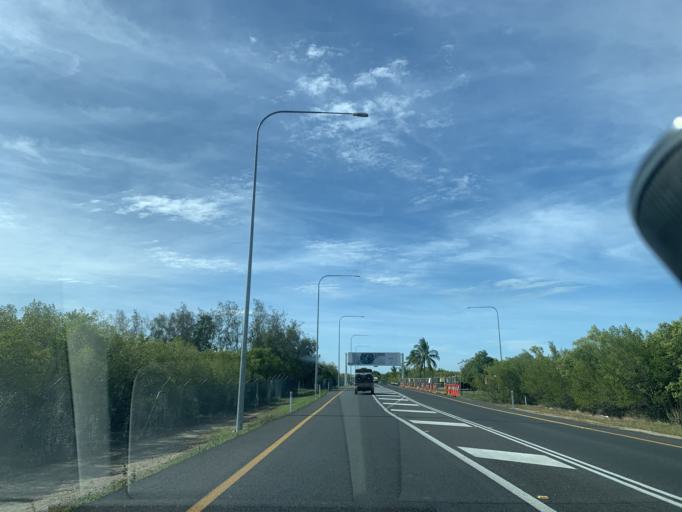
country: AU
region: Queensland
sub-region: Cairns
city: Cairns
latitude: -16.8846
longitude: 145.7614
